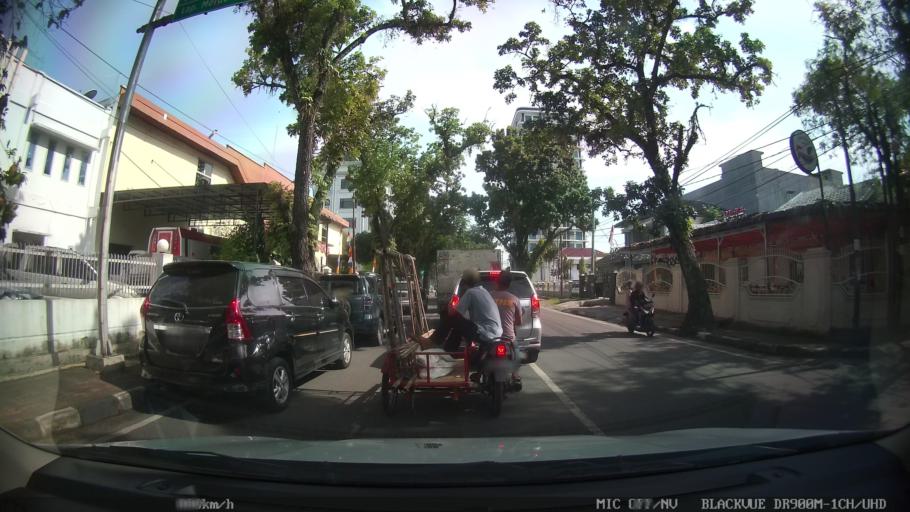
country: ID
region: North Sumatra
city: Medan
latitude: 3.5763
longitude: 98.6574
